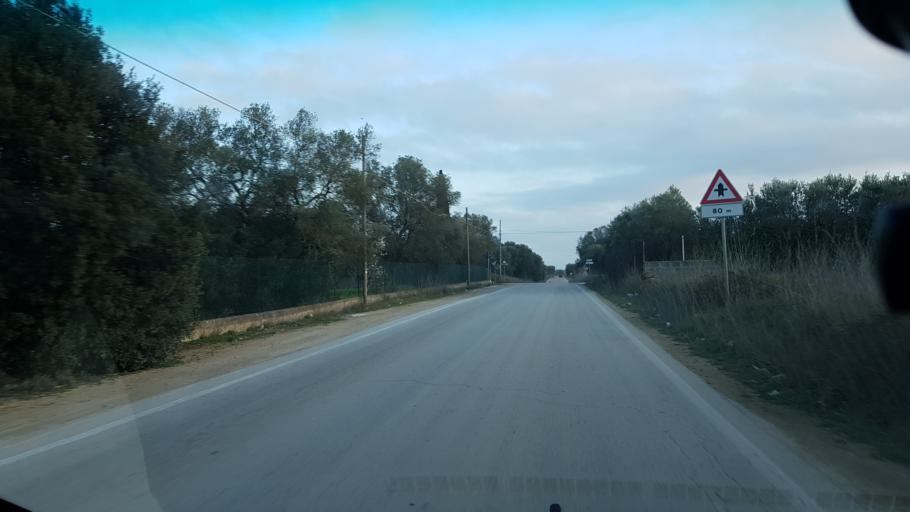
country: IT
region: Apulia
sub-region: Provincia di Brindisi
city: San Vito dei Normanni
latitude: 40.6422
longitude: 17.7783
